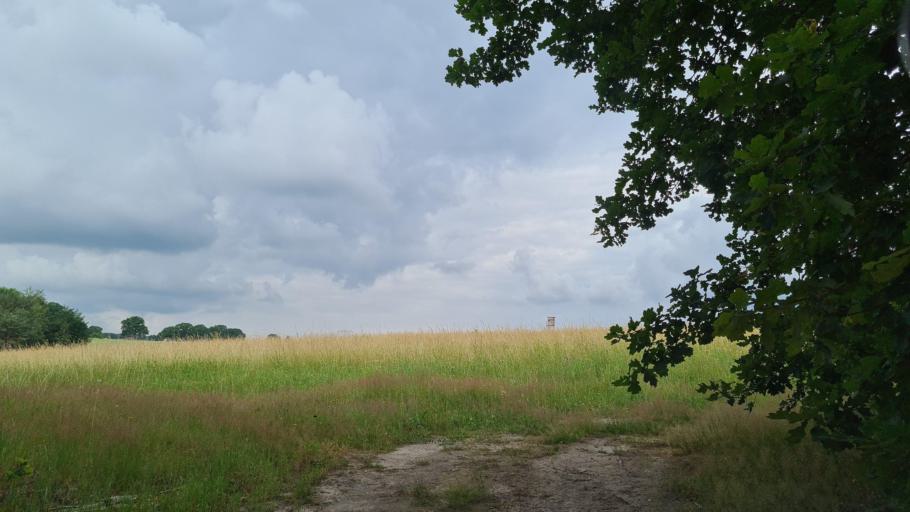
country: DE
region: Brandenburg
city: Crinitz
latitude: 51.7400
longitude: 13.7409
